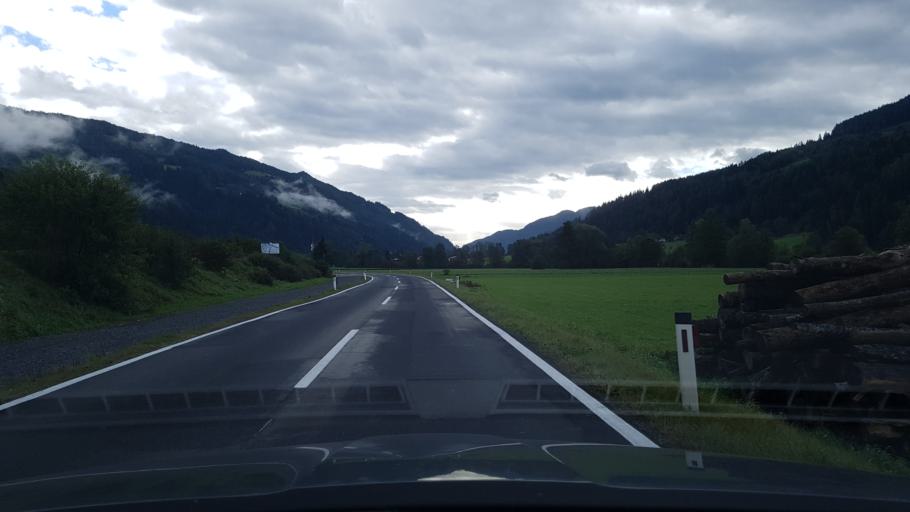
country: AT
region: Styria
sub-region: Politischer Bezirk Murau
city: Winklern bei Oberwolz
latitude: 47.1801
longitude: 14.2136
